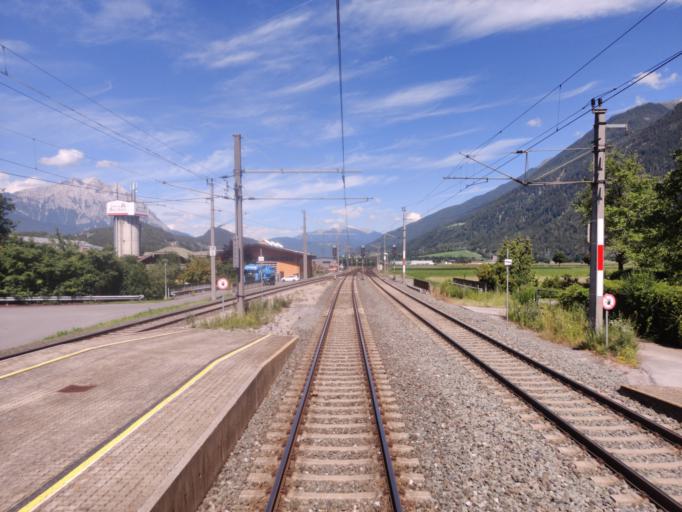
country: AT
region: Tyrol
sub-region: Politischer Bezirk Imst
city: Silz
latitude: 47.2706
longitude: 10.9391
